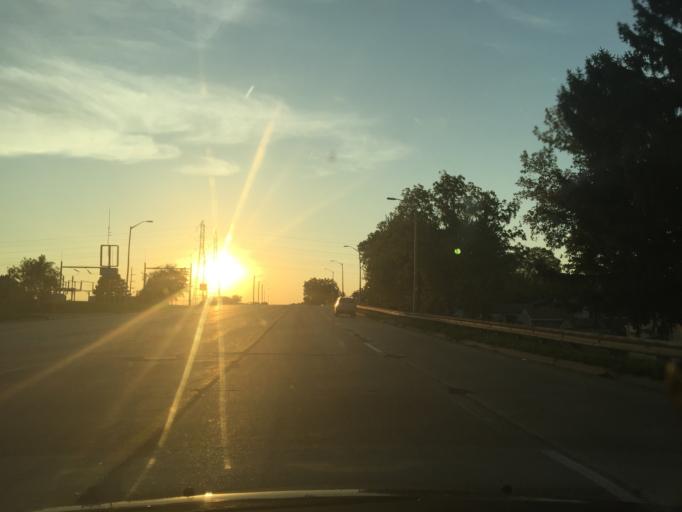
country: US
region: Michigan
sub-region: Oakland County
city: Pontiac
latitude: 42.6490
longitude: -83.2568
